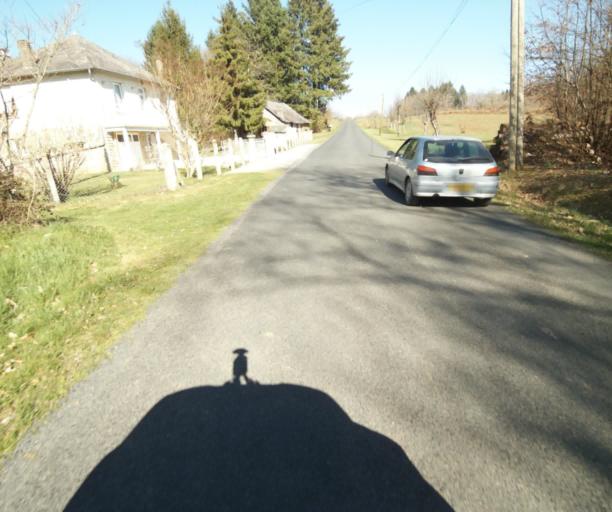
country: FR
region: Limousin
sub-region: Departement de la Correze
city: Chamboulive
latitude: 45.4321
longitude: 1.6627
